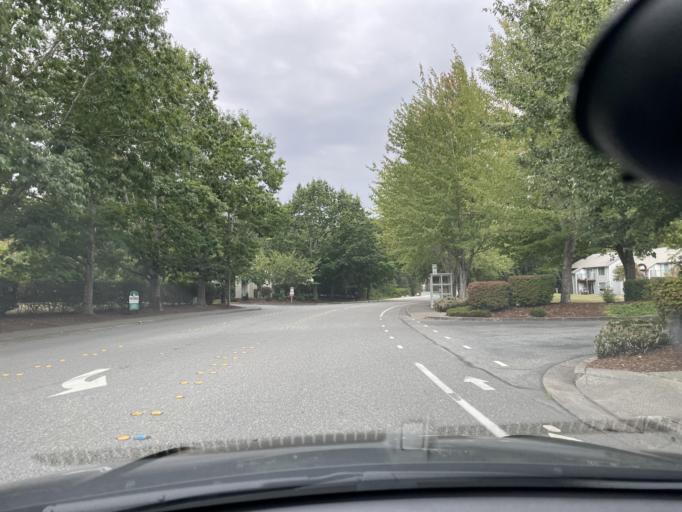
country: US
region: Washington
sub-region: Whatcom County
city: Bellingham
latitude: 48.8044
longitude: -122.5004
